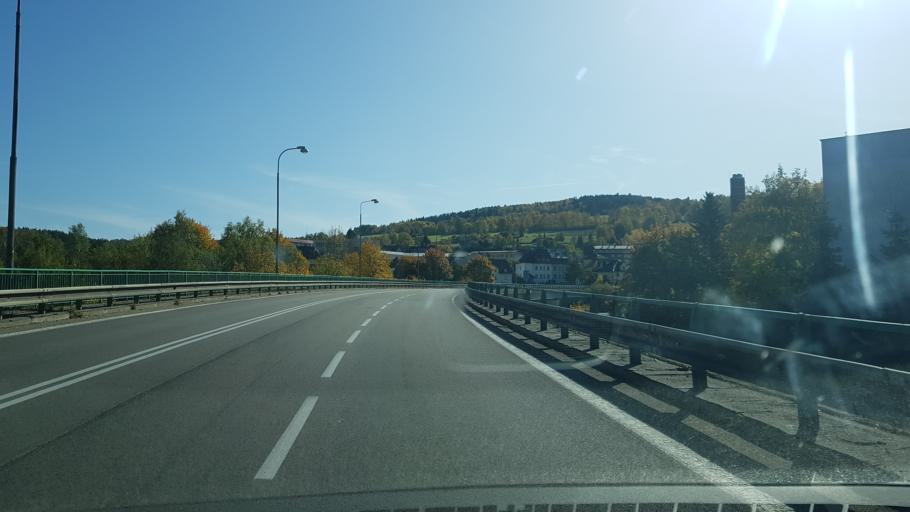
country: CZ
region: Jihocesky
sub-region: Okres Prachatice
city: Vimperk
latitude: 49.0579
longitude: 13.7856
